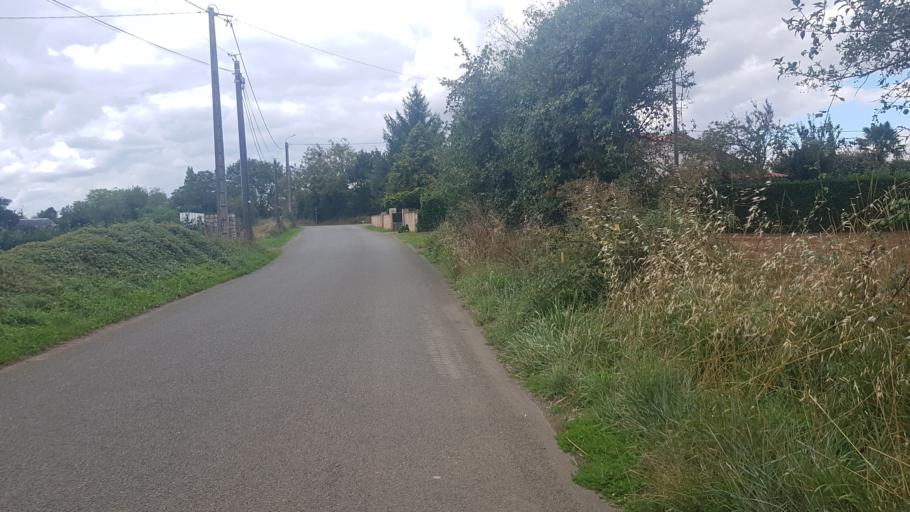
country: FR
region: Poitou-Charentes
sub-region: Departement des Deux-Sevres
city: Vouille
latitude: 46.3353
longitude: -0.3610
